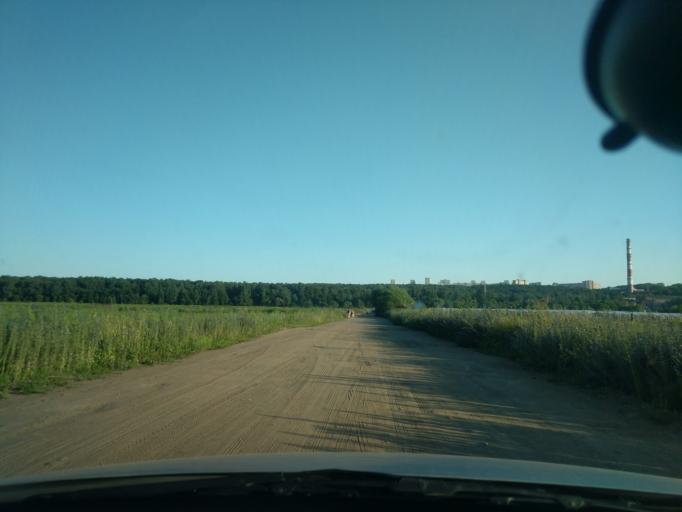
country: RU
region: Moskovskaya
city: Pushchino
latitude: 54.8477
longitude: 37.6405
